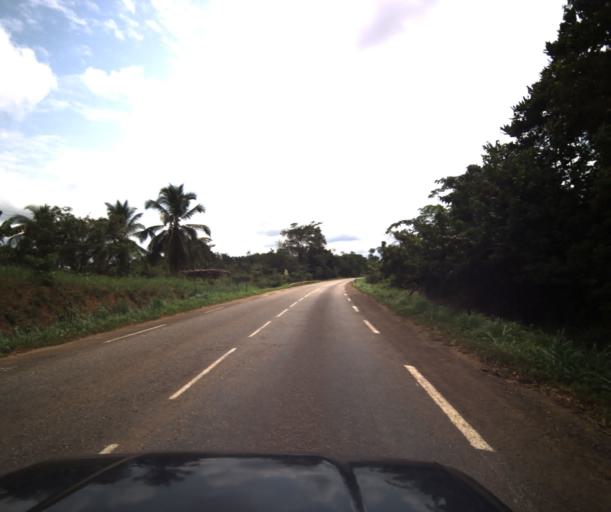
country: CM
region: Centre
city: Eseka
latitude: 3.8675
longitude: 10.6038
